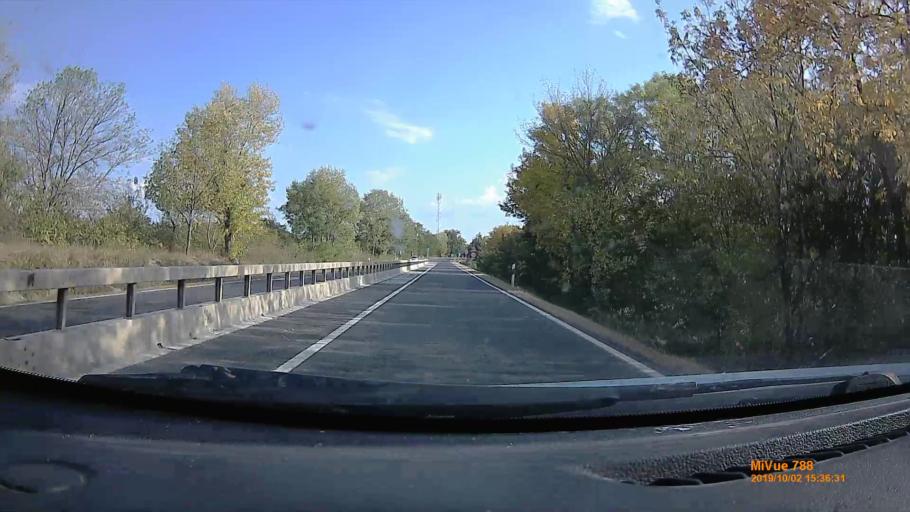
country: HU
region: Heves
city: Egerszalok
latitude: 47.8472
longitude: 20.3709
